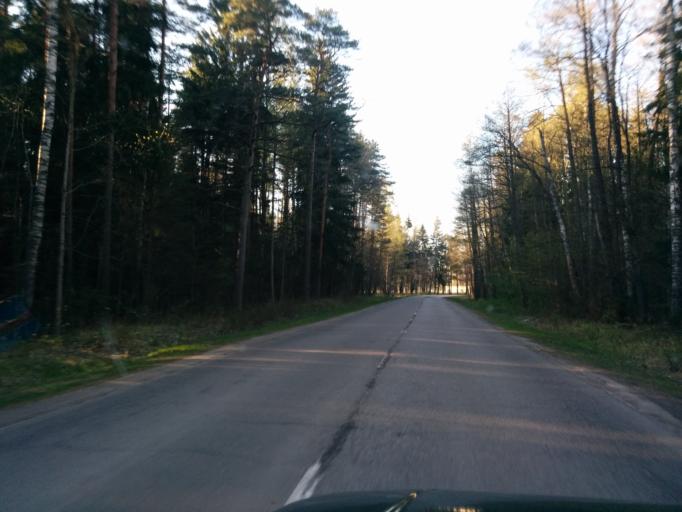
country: LV
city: Tireli
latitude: 56.9362
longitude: 23.4863
